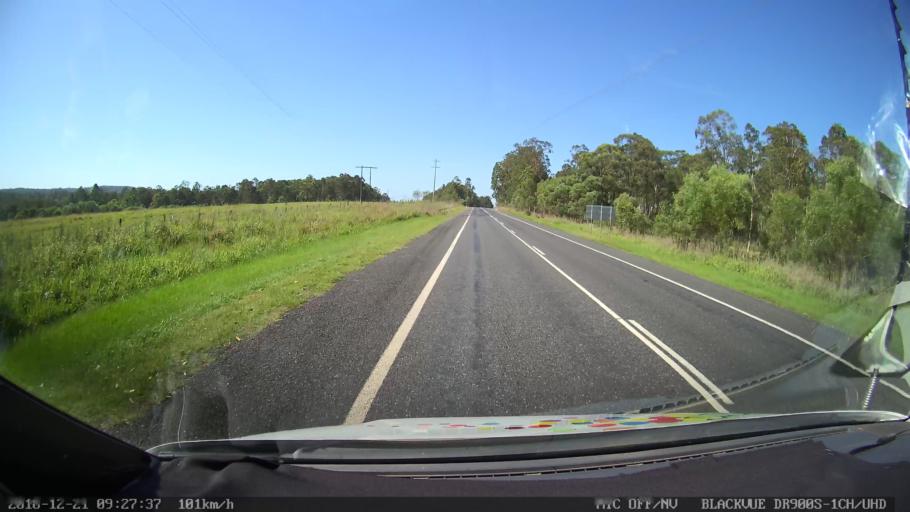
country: AU
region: New South Wales
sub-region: Clarence Valley
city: Maclean
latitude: -29.4053
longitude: 152.9893
